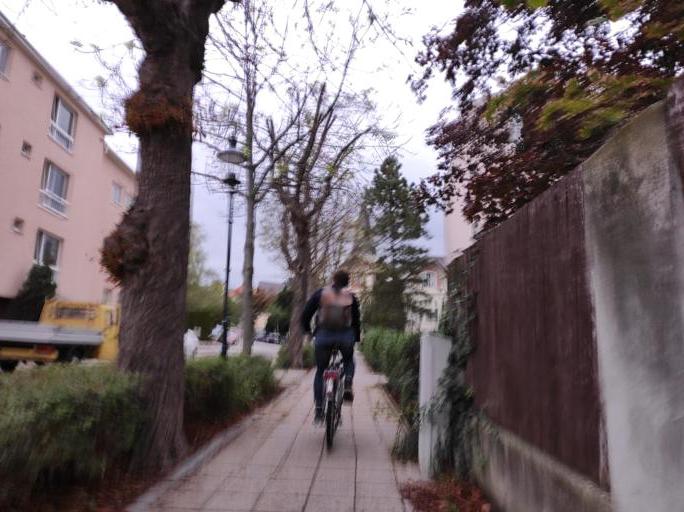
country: AT
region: Lower Austria
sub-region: Politischer Bezirk Baden
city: Baden
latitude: 48.0120
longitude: 16.2441
